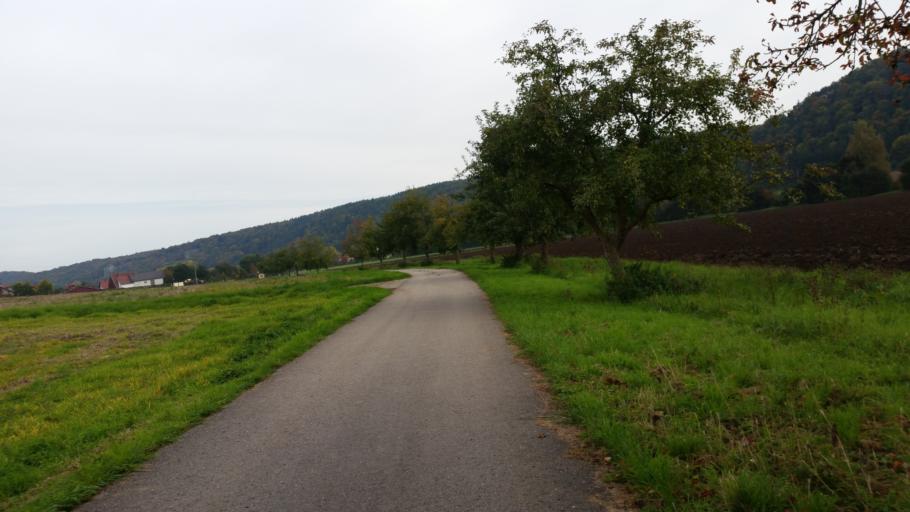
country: DE
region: Bavaria
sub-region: Upper Bavaria
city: Walting
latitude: 48.9263
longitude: 11.3410
